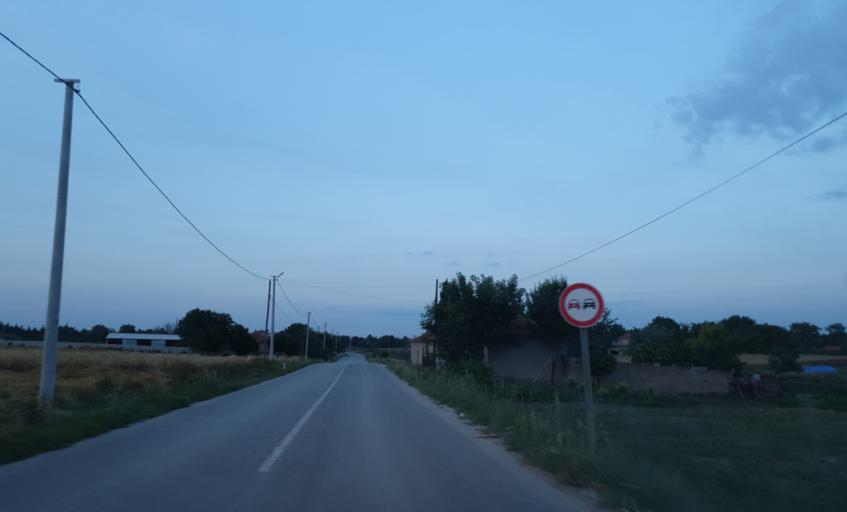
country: TR
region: Tekirdag
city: Beyazkoy
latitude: 41.4340
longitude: 27.6926
